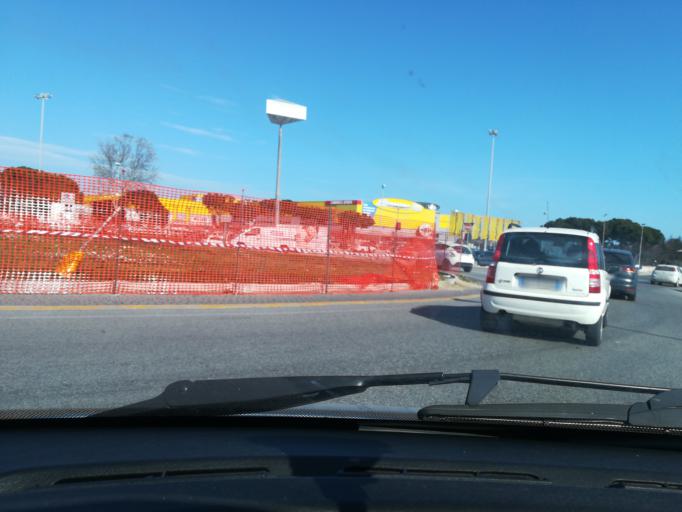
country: IT
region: The Marches
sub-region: Provincia di Macerata
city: Santa Maria Apparente
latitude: 43.2932
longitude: 13.7065
